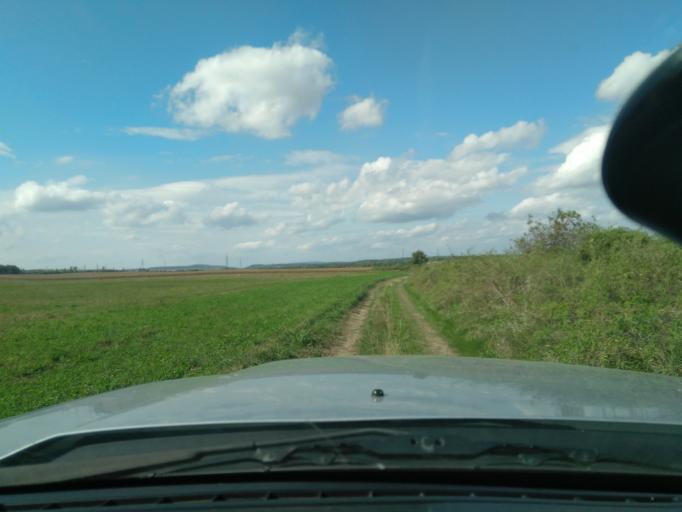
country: HU
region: Fejer
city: Bicske
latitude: 47.4720
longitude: 18.6716
